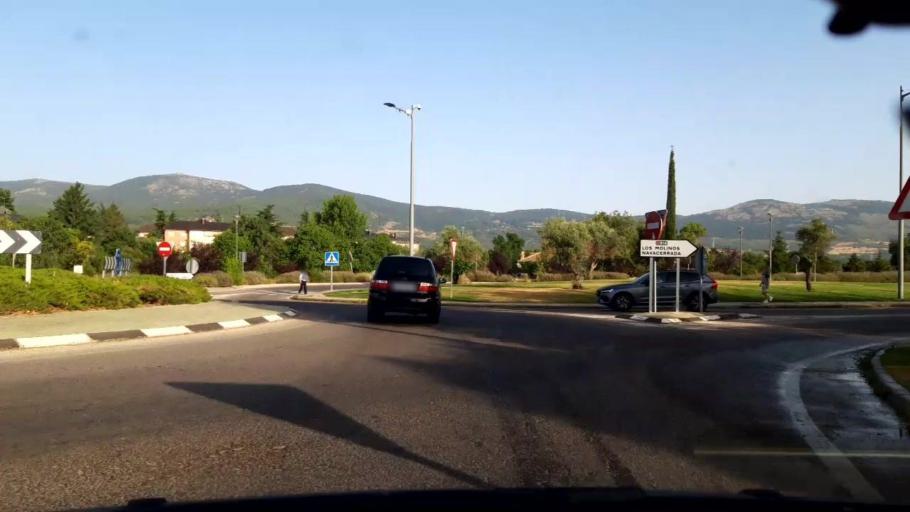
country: ES
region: Madrid
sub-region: Provincia de Madrid
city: Guadarrama
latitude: 40.6758
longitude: -4.0825
